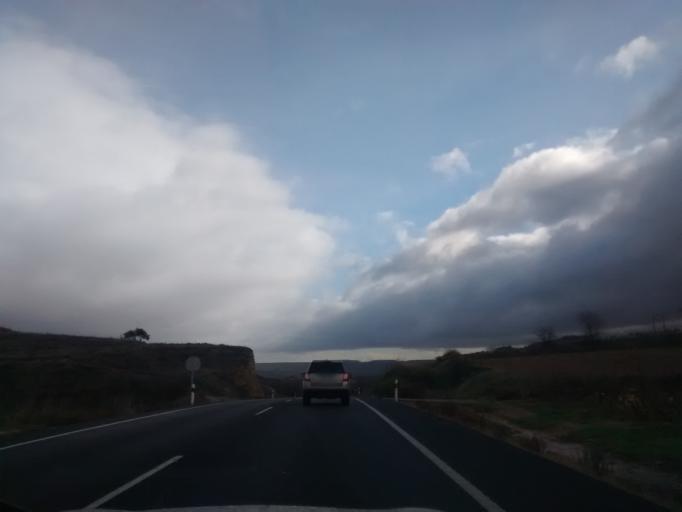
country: ES
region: La Rioja
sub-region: Provincia de La Rioja
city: San Asensio
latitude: 42.5108
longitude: -2.7243
